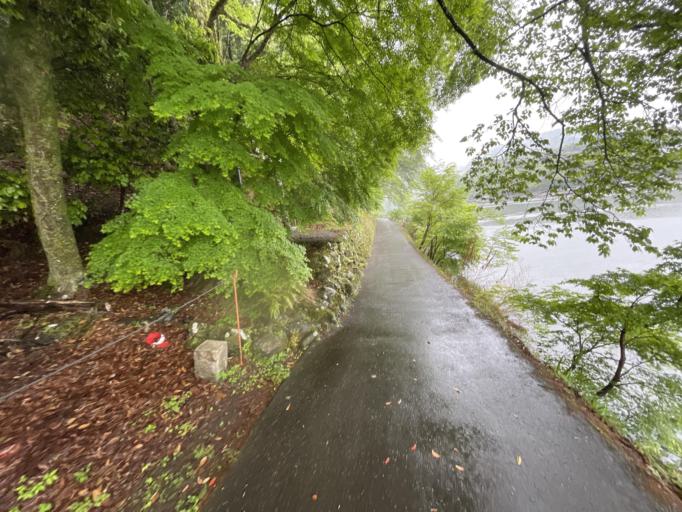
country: JP
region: Kyoto
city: Muko
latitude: 35.0122
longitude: 135.6751
